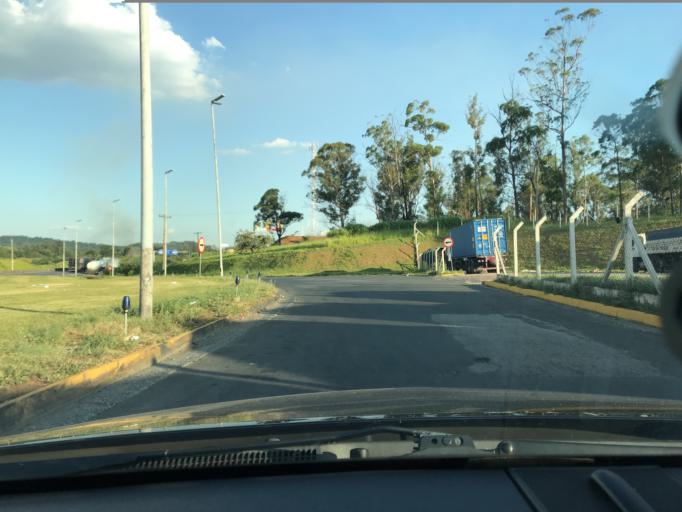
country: BR
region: Sao Paulo
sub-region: Vinhedo
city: Vinhedo
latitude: -23.0408
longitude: -47.0668
